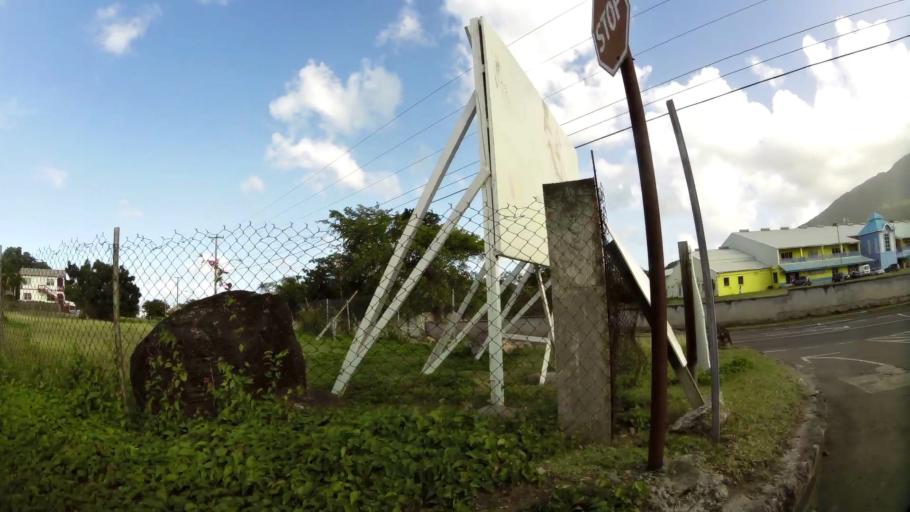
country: KN
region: Saint Paul Charlestown
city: Charlestown
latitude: 17.1314
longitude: -62.6216
